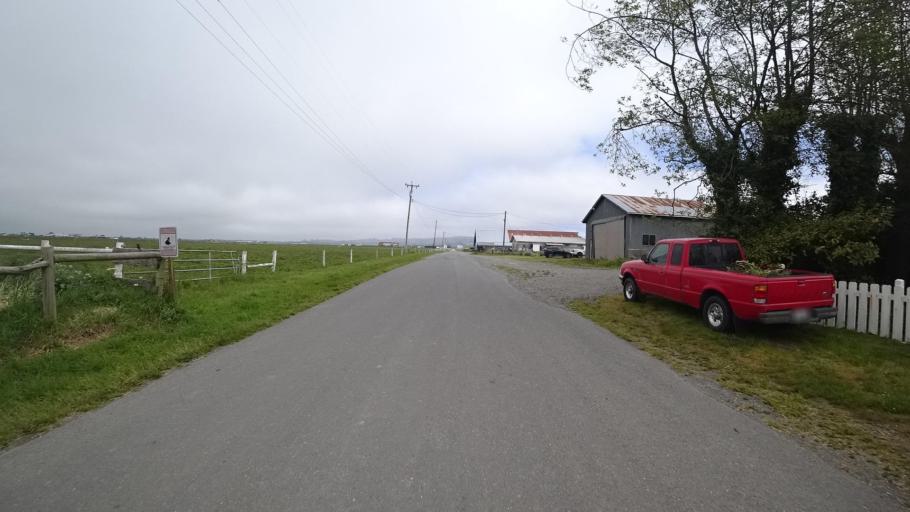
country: US
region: California
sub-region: Humboldt County
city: Fortuna
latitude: 40.5703
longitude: -124.1877
